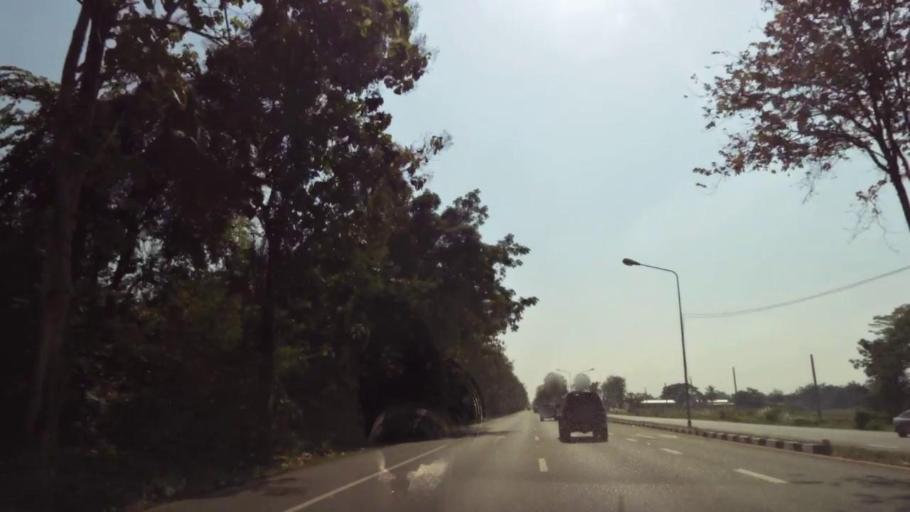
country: TH
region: Phichit
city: Bueng Na Rang
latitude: 16.0911
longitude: 100.1252
